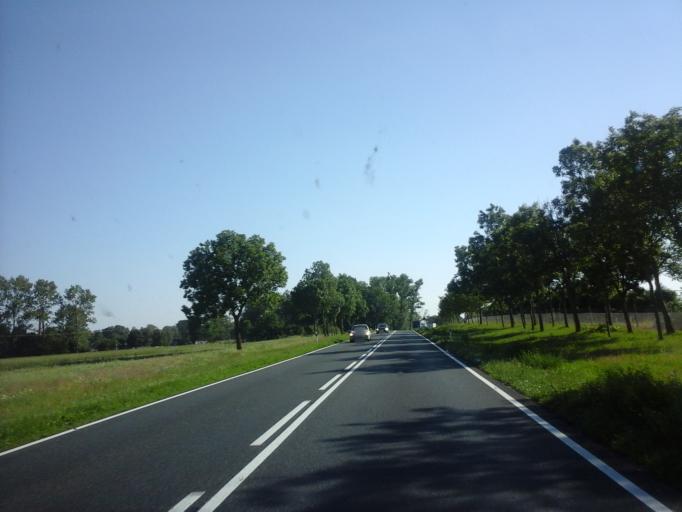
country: PL
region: West Pomeranian Voivodeship
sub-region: Powiat gryficki
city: Ploty
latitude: 53.7533
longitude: 15.2231
